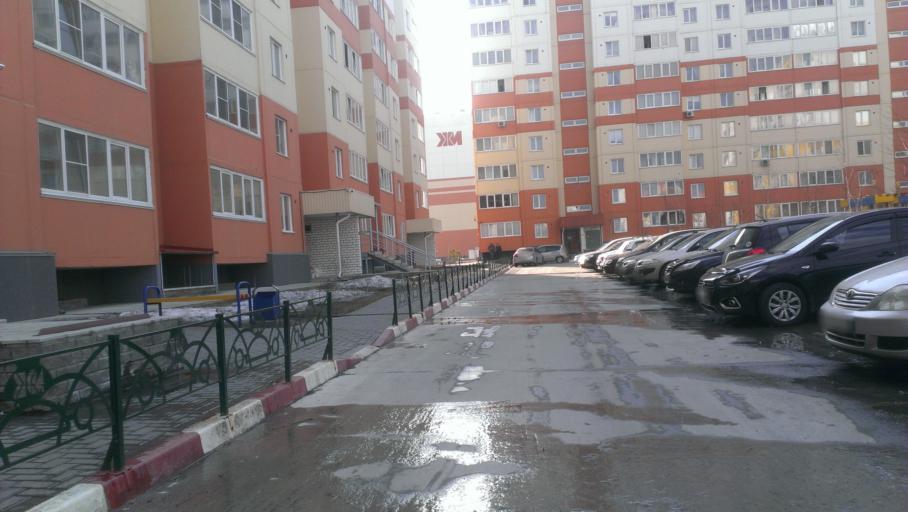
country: RU
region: Altai Krai
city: Novosilikatnyy
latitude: 53.3255
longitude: 83.6765
